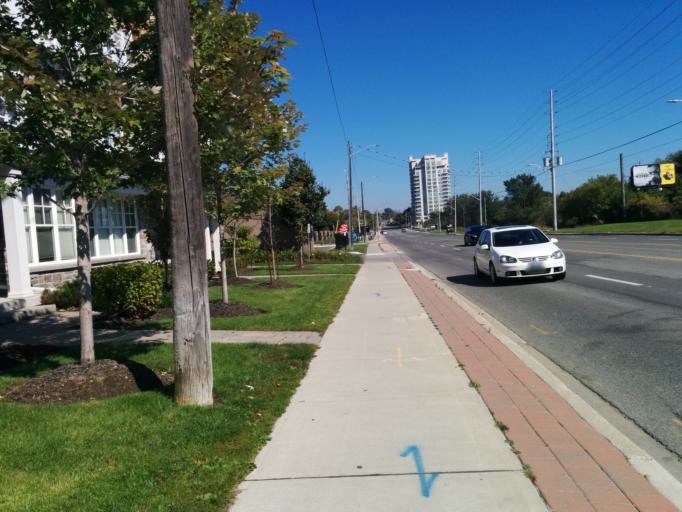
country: CA
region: Ontario
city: Etobicoke
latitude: 43.5864
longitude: -79.5490
